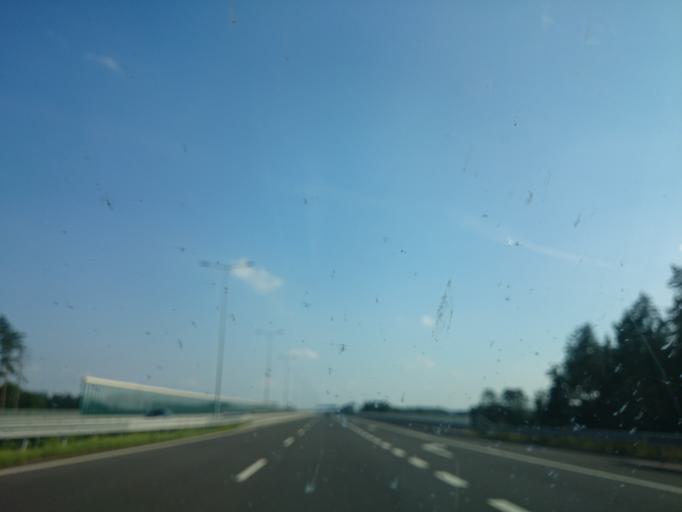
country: PL
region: Silesian Voivodeship
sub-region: Powiat rybnicki
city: Stanowice
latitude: 50.0870
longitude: 18.6630
